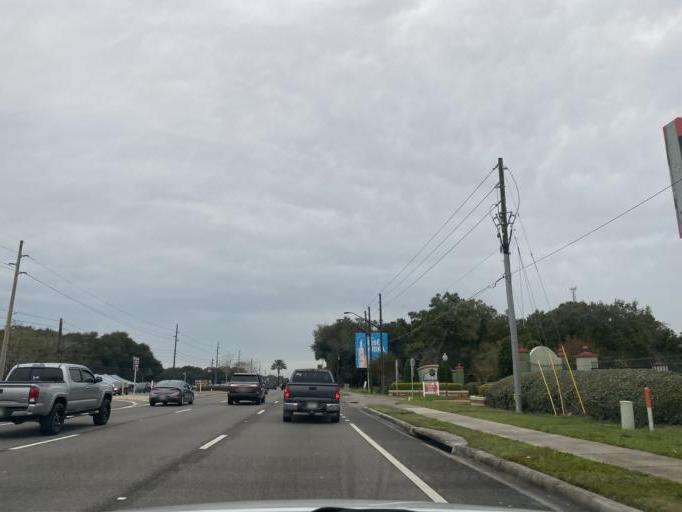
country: US
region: Florida
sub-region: Orange County
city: Winter Garden
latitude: 28.5512
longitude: -81.5956
